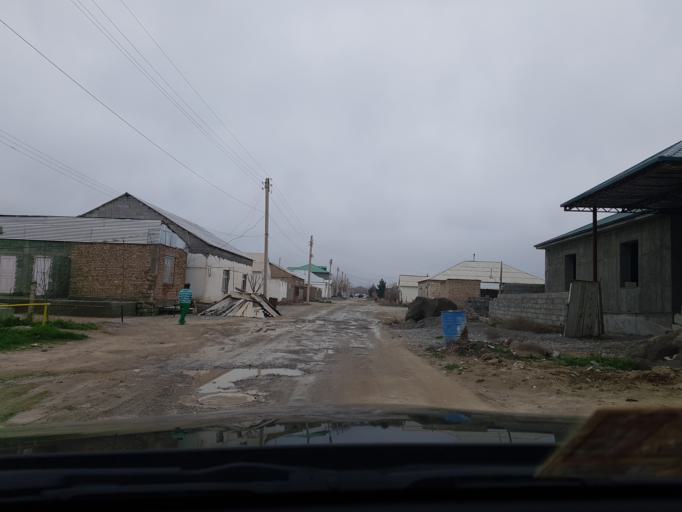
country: TM
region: Ahal
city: Abadan
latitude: 38.1448
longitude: 57.9491
